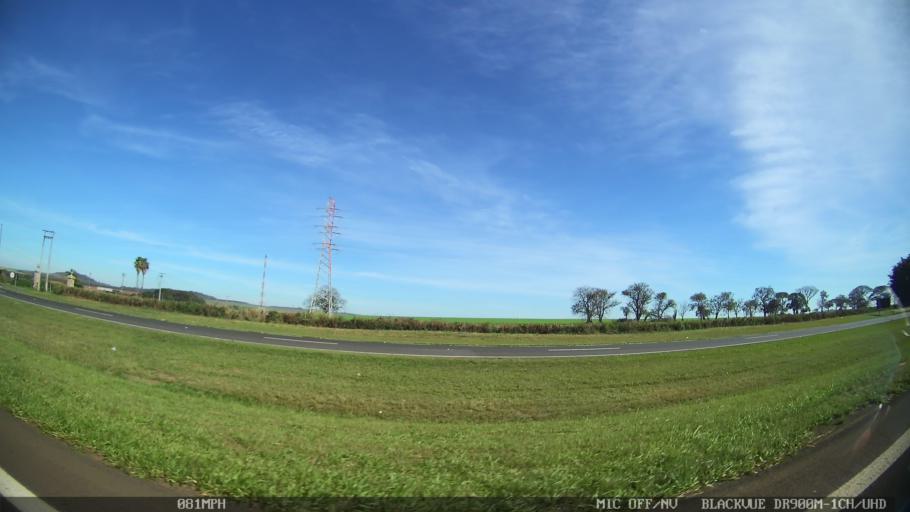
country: BR
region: Sao Paulo
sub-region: Araras
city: Araras
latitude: -22.2849
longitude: -47.3934
